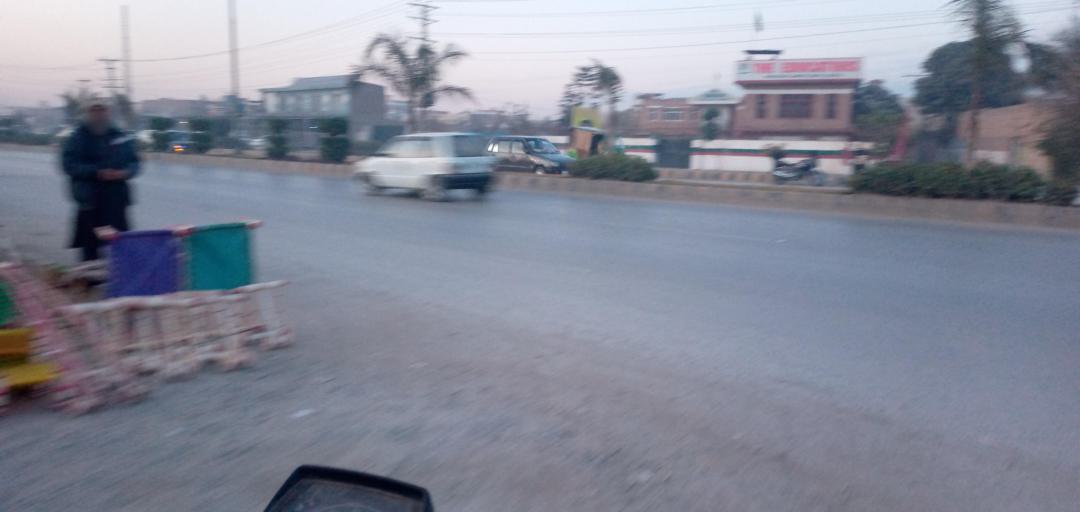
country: PK
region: Khyber Pakhtunkhwa
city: Peshawar
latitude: 34.0296
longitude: 71.6122
